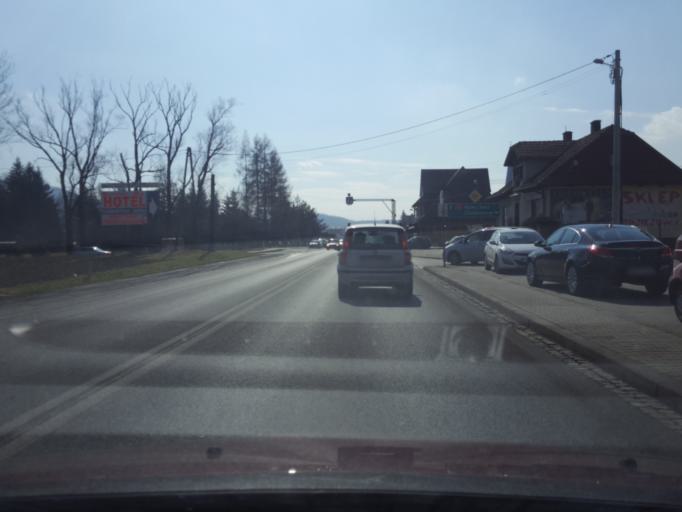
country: PL
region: Lesser Poland Voivodeship
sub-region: Powiat nowosadecki
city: Lososina Dolna
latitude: 49.7104
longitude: 20.6433
